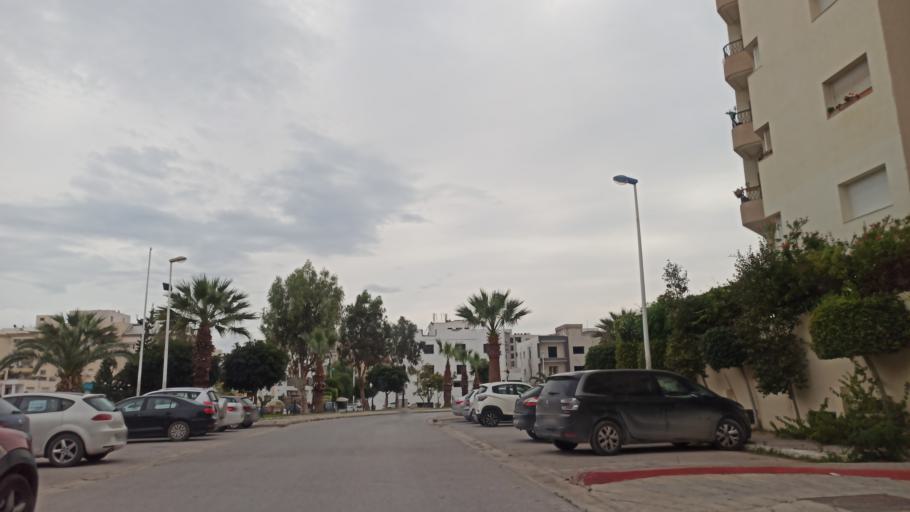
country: TN
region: Tunis
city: La Goulette
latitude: 36.8590
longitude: 10.2653
